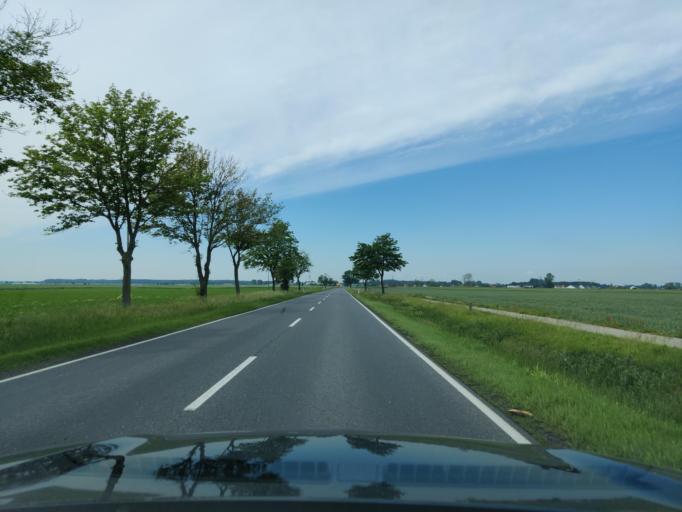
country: PL
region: Greater Poland Voivodeship
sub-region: Powiat poznanski
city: Steszew
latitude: 52.2529
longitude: 16.6358
